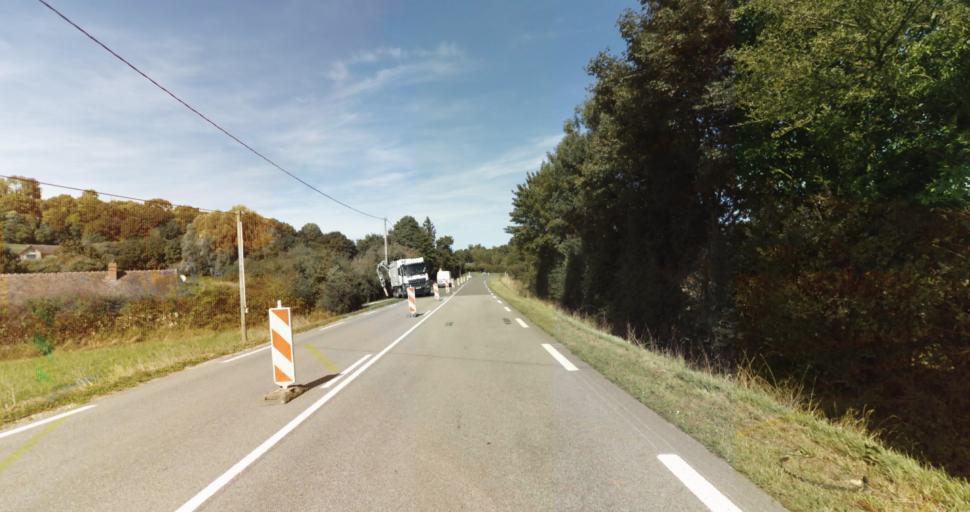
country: FR
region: Lower Normandy
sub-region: Departement de l'Orne
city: Gace
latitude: 48.7274
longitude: 0.2348
